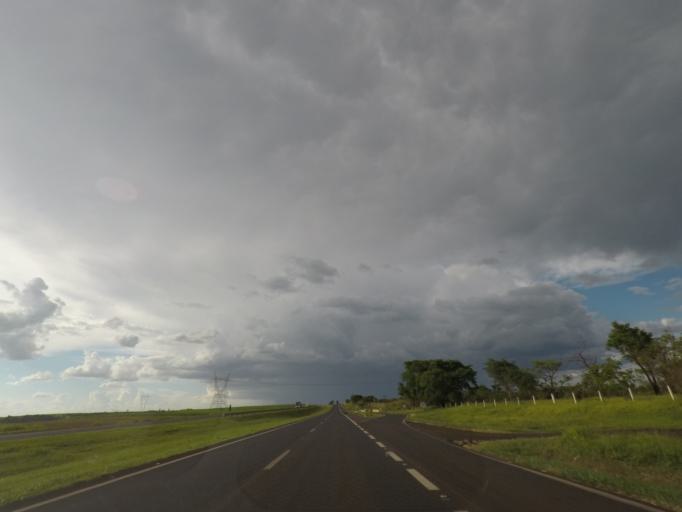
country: BR
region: Sao Paulo
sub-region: Jardinopolis
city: Jardinopolis
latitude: -21.0227
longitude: -47.8390
